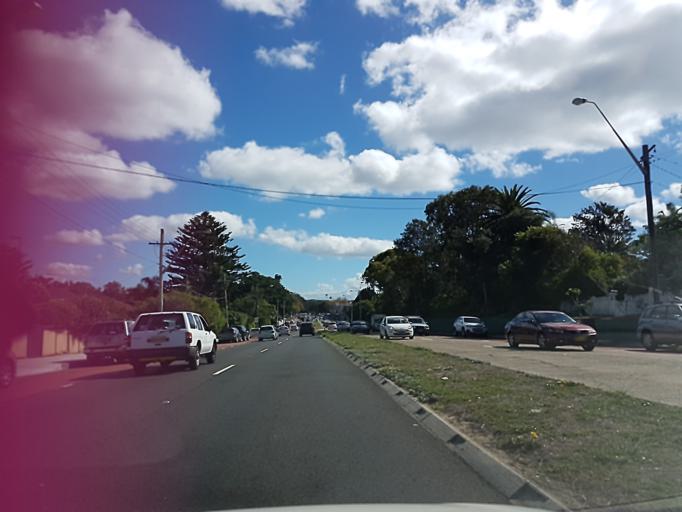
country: AU
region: New South Wales
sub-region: Warringah
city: Narrabeen
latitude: -33.7166
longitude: 151.2974
